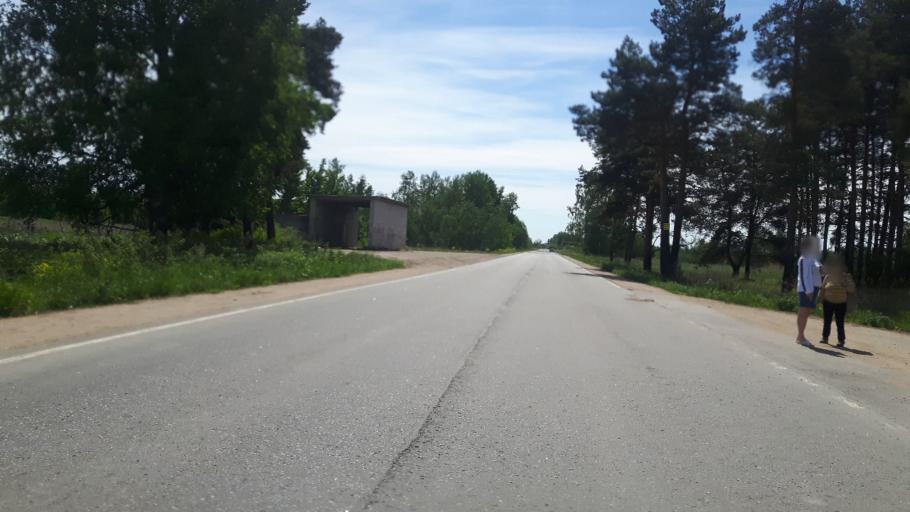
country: RU
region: Leningrad
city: Ust'-Luga
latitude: 59.5775
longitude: 28.1756
